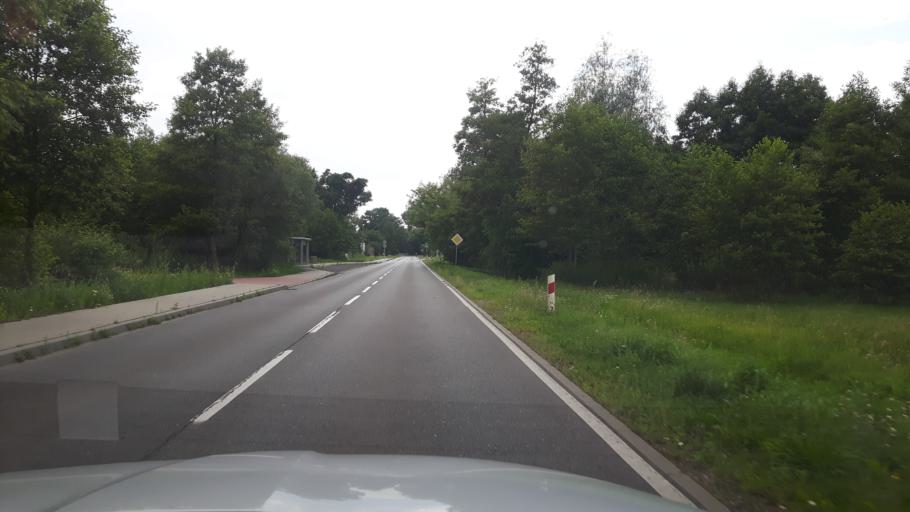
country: PL
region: Masovian Voivodeship
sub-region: Powiat wolominski
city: Jasienica
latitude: 52.3793
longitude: 21.4096
